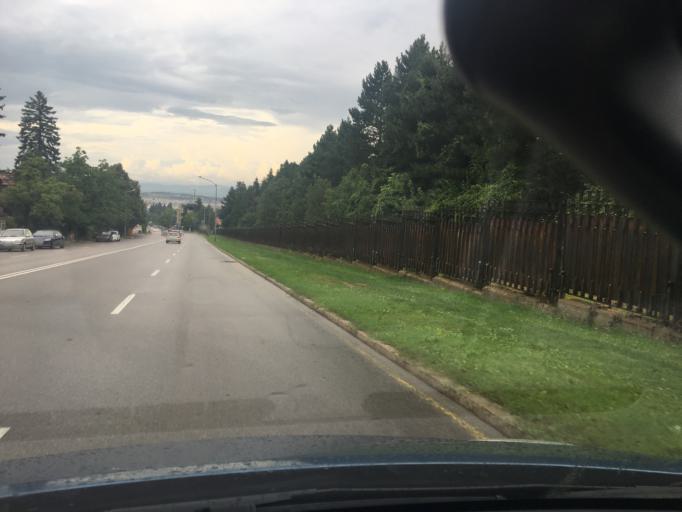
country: BG
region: Sofia-Capital
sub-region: Stolichna Obshtina
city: Sofia
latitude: 42.6527
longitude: 23.2661
